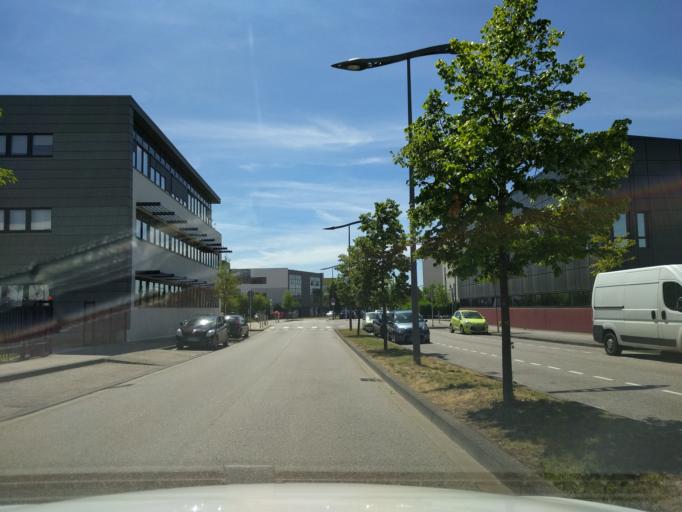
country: FR
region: Lorraine
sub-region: Departement de la Moselle
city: Saint-Julien-les-Metz
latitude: 49.1165
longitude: 6.2323
